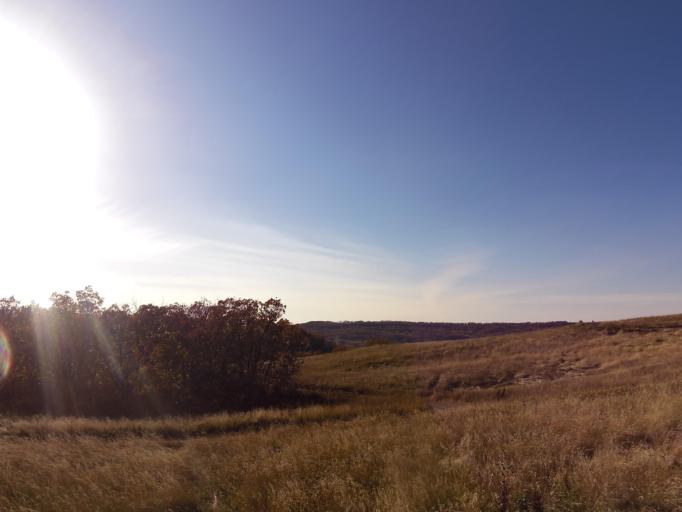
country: CA
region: Manitoba
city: Morden
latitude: 48.9385
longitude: -98.0608
